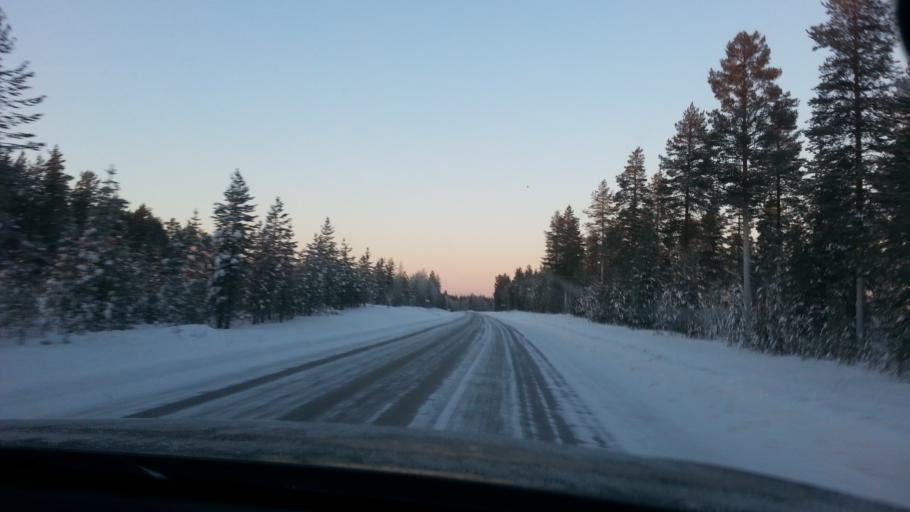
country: FI
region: Lapland
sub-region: Rovaniemi
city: Rovaniemi
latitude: 66.7768
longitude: 25.4547
